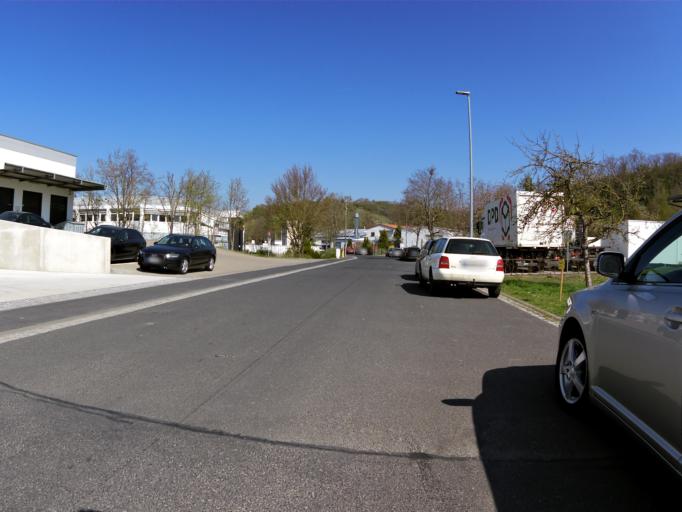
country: DE
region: Bavaria
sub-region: Regierungsbezirk Unterfranken
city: Rottendorf
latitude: 49.7917
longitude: 10.0370
